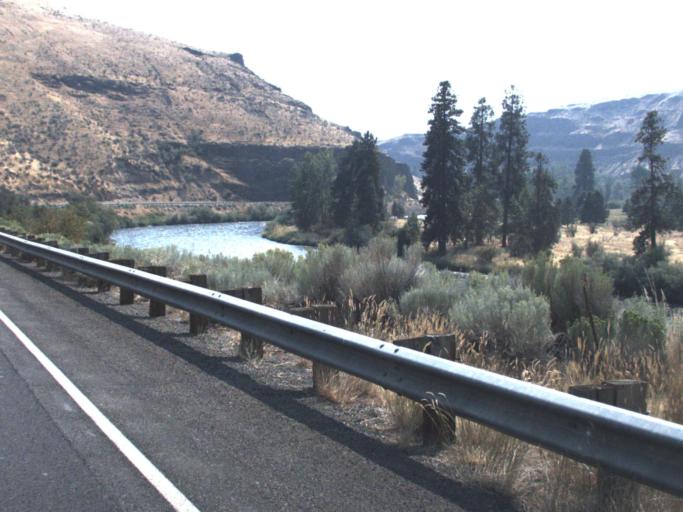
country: US
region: Washington
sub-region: Kittitas County
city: Kittitas
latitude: 46.8522
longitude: -120.4628
